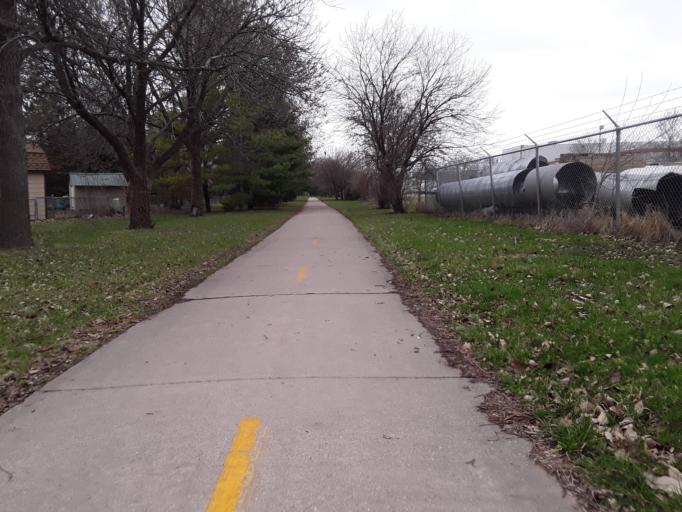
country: US
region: Nebraska
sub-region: Lancaster County
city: Lincoln
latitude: 40.8459
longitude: -96.6603
